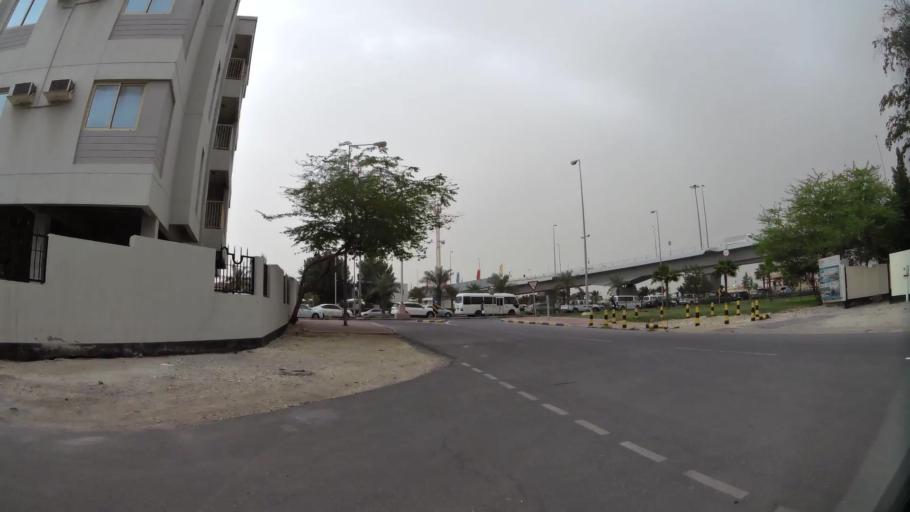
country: BH
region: Northern
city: Madinat `Isa
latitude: 26.1698
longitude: 50.5440
